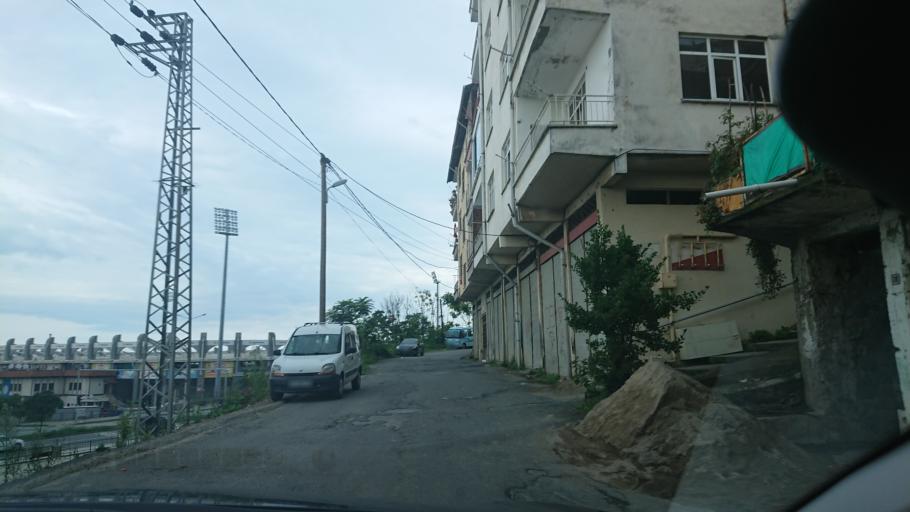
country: TR
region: Rize
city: Gundogdu
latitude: 41.0399
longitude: 40.5724
